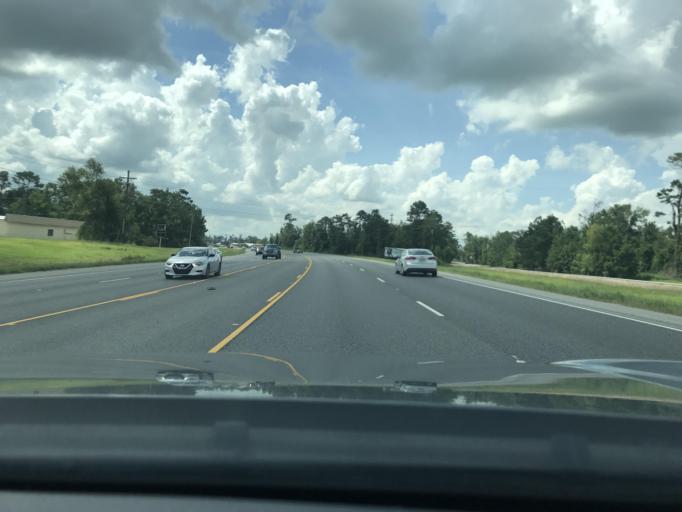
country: US
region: Louisiana
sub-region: Calcasieu Parish
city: Moss Bluff
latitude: 30.3198
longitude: -93.2000
